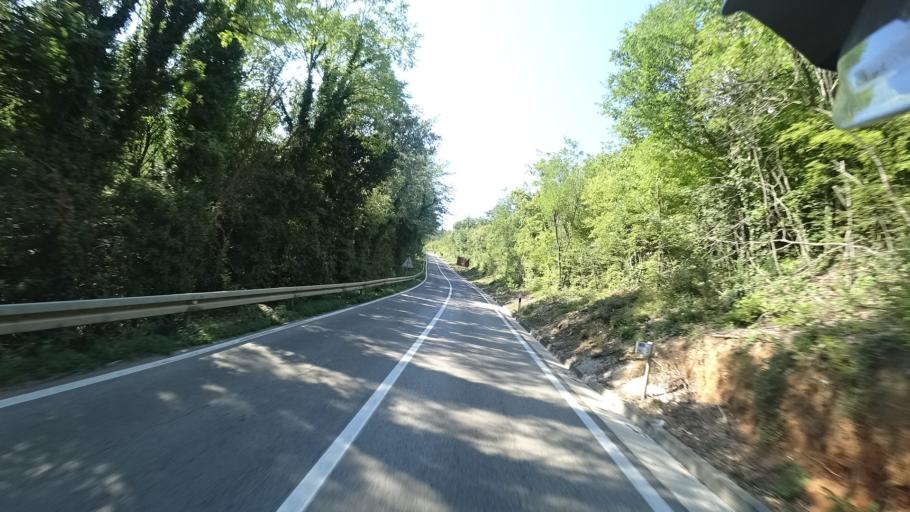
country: HR
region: Sibensko-Kniniska
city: Knin
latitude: 44.0214
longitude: 16.1956
